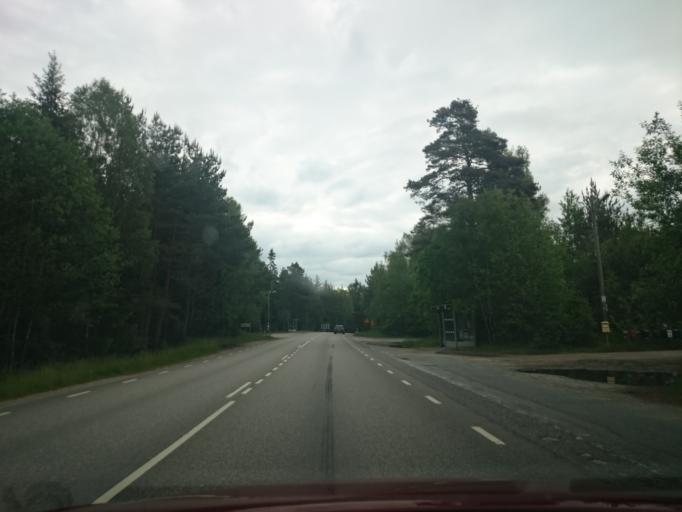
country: SE
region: Vaestra Goetaland
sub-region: Harryda Kommun
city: Hindas
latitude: 57.6976
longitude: 12.3712
